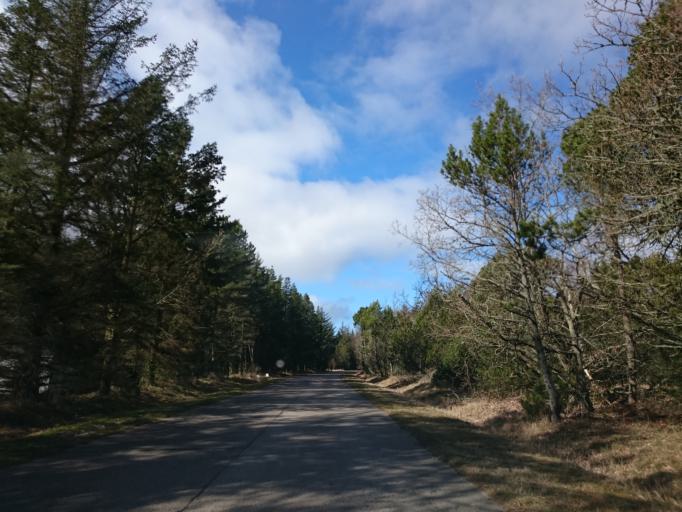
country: DK
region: North Denmark
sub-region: Frederikshavn Kommune
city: Skagen
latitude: 57.6542
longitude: 10.4237
